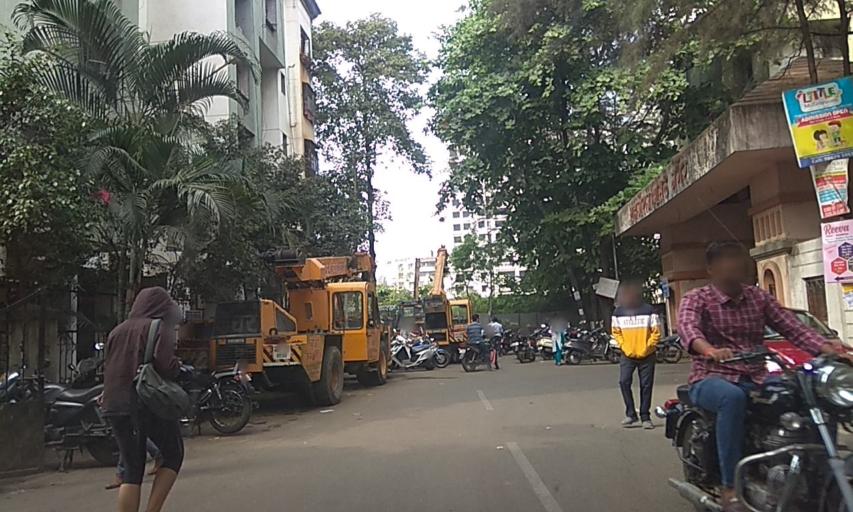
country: IN
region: Maharashtra
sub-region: Pune Division
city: Pune
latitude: 18.5029
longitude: 73.9319
